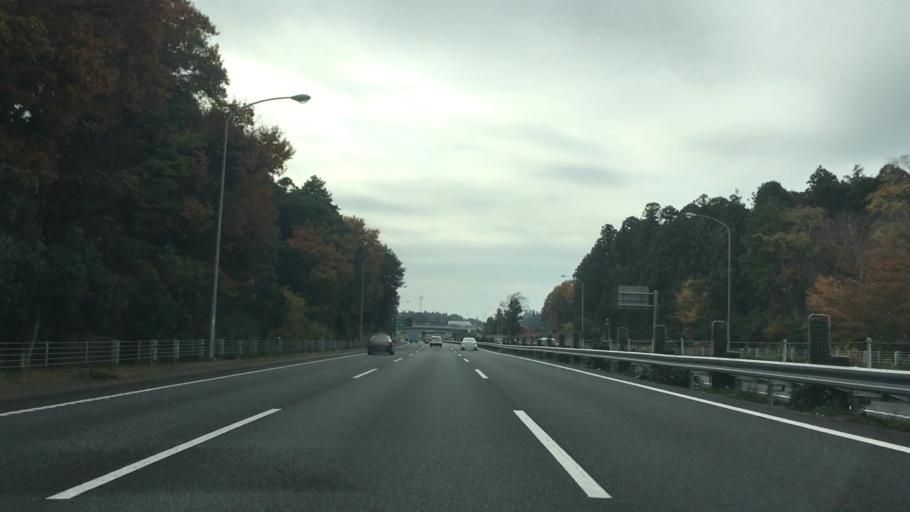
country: JP
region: Chiba
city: Shisui
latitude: 35.7372
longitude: 140.3030
